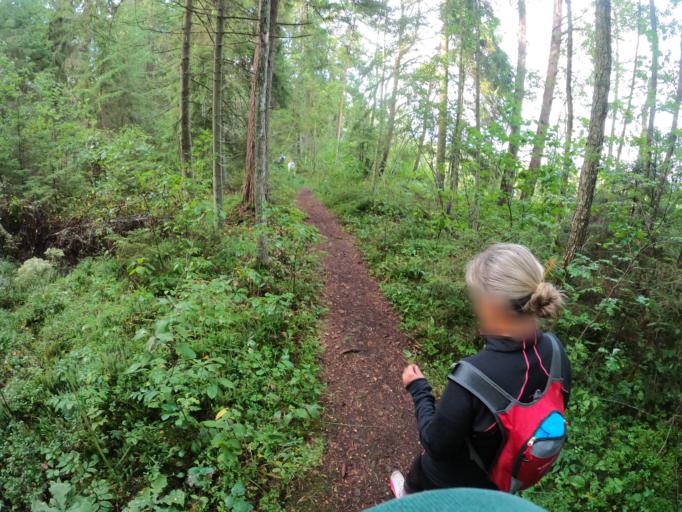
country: LV
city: Tireli
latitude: 56.9655
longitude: 23.5361
